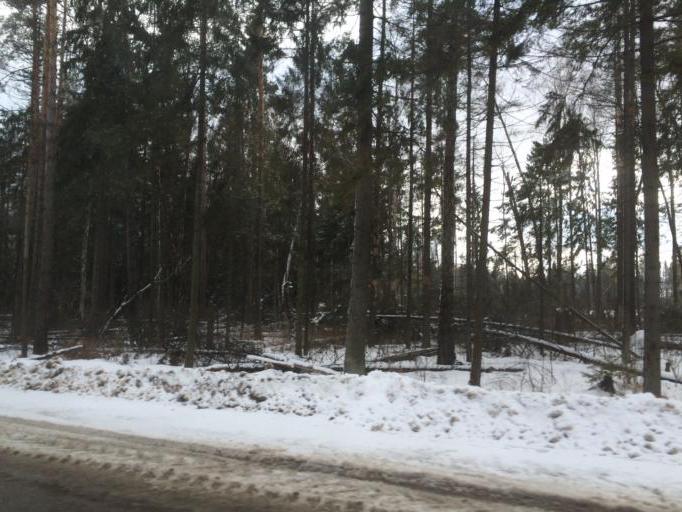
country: RU
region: Moskovskaya
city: Petrovo-Dal'neye
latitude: 55.7966
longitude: 37.1439
